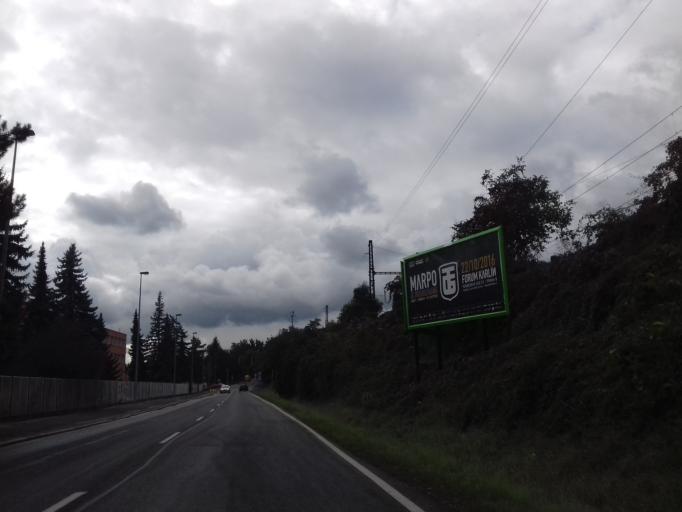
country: CZ
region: Praha
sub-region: Praha 12
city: Modrany
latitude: 49.9895
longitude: 14.3692
